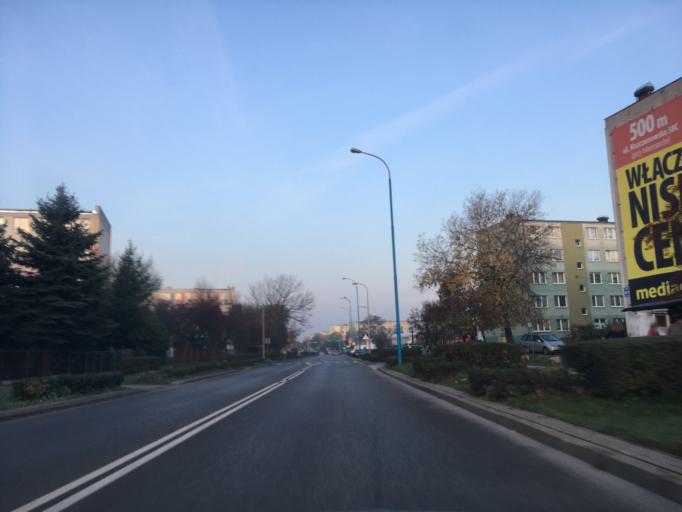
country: PL
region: Lodz Voivodeship
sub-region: Skierniewice
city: Skierniewice
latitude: 51.9552
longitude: 20.1556
